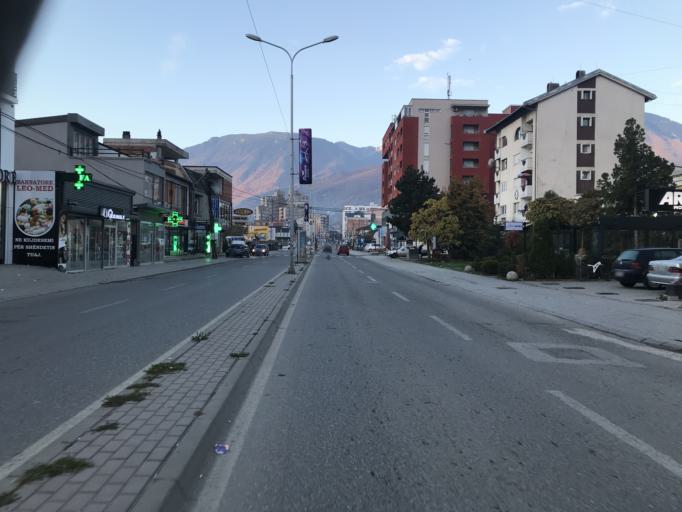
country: XK
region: Pec
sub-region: Komuna e Pejes
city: Peje
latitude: 42.6659
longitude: 20.3012
